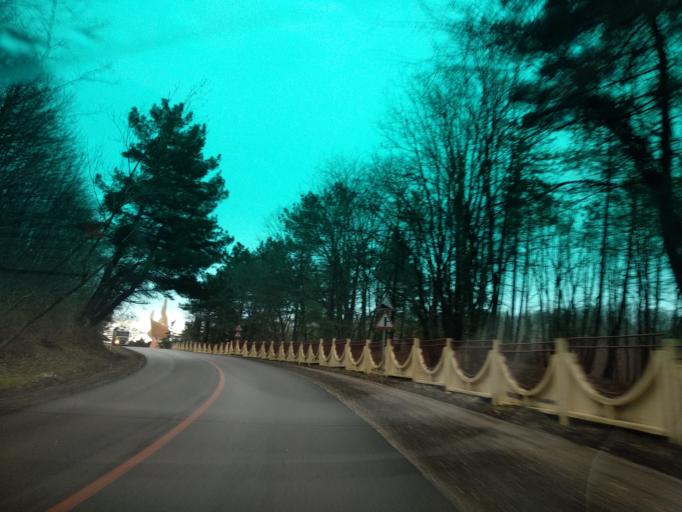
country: RU
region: Krasnodarskiy
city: Novomikhaylovskiy
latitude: 44.2570
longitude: 38.8292
